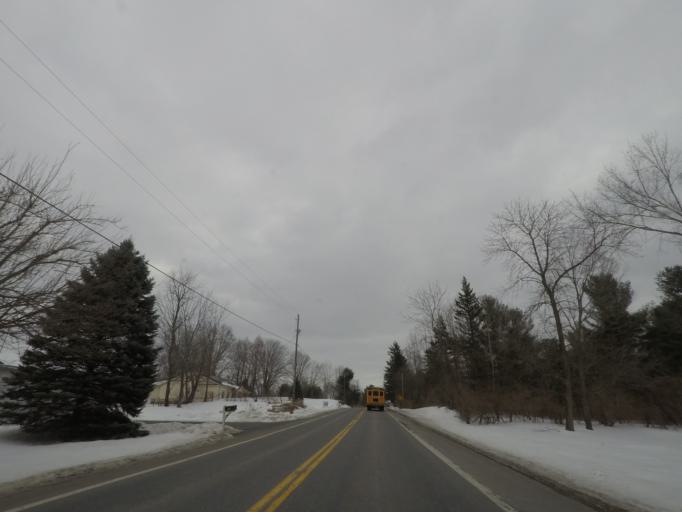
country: US
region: New York
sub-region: Saratoga County
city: Stillwater
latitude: 42.9669
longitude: -73.6816
